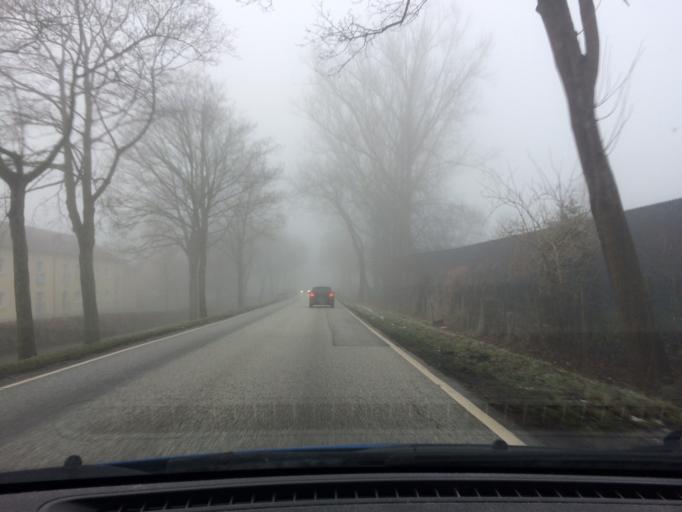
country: DE
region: Schleswig-Holstein
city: Lauenburg
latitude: 53.3778
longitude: 10.5464
